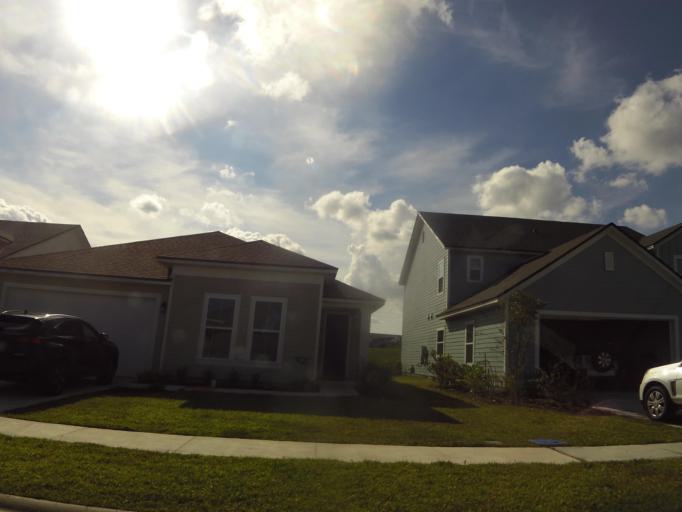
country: US
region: Florida
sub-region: Saint Johns County
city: Saint Augustine
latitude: 29.9214
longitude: -81.4950
